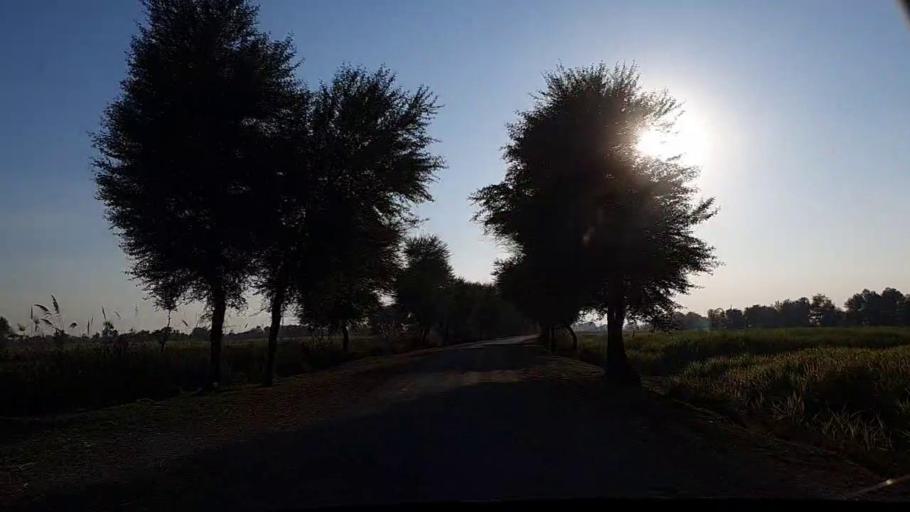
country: PK
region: Sindh
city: Sobhadero
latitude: 27.4183
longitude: 68.4035
